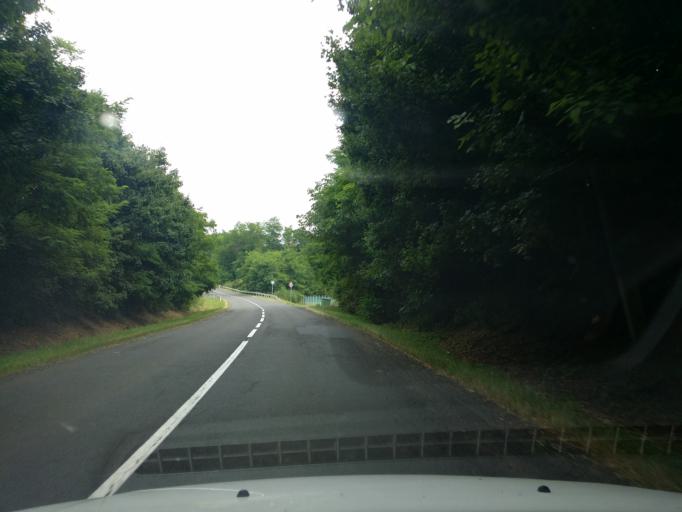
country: HU
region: Nograd
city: Bercel
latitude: 47.9454
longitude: 19.3627
